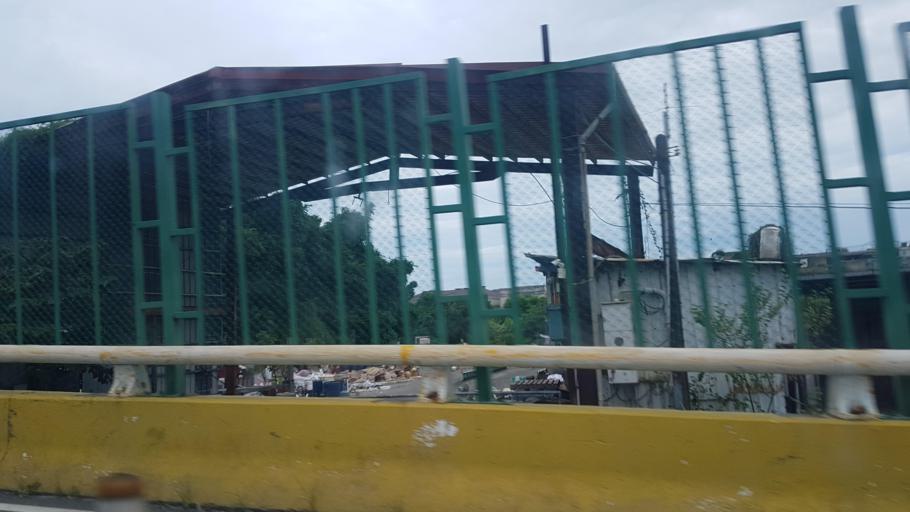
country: TW
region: Taiwan
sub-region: Hualien
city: Hualian
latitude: 23.9811
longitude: 121.5932
